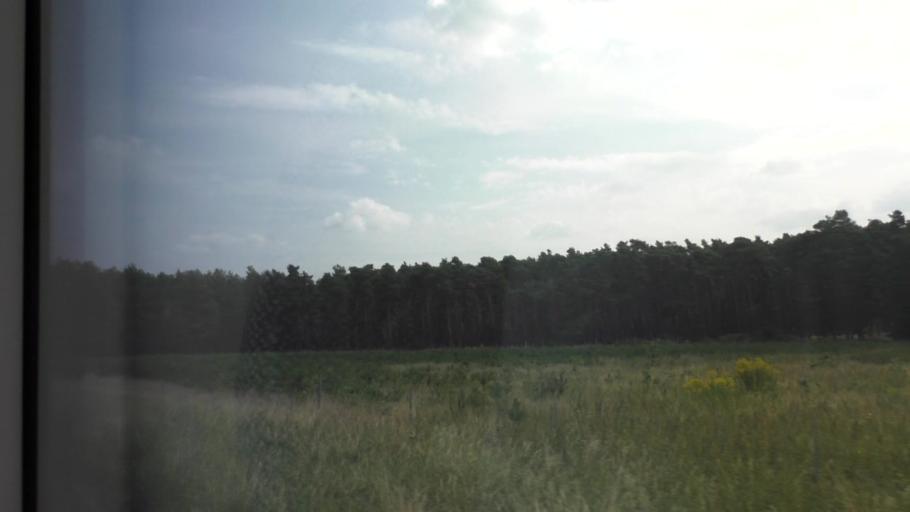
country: DE
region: Brandenburg
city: Mixdorf
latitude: 52.1625
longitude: 14.3397
